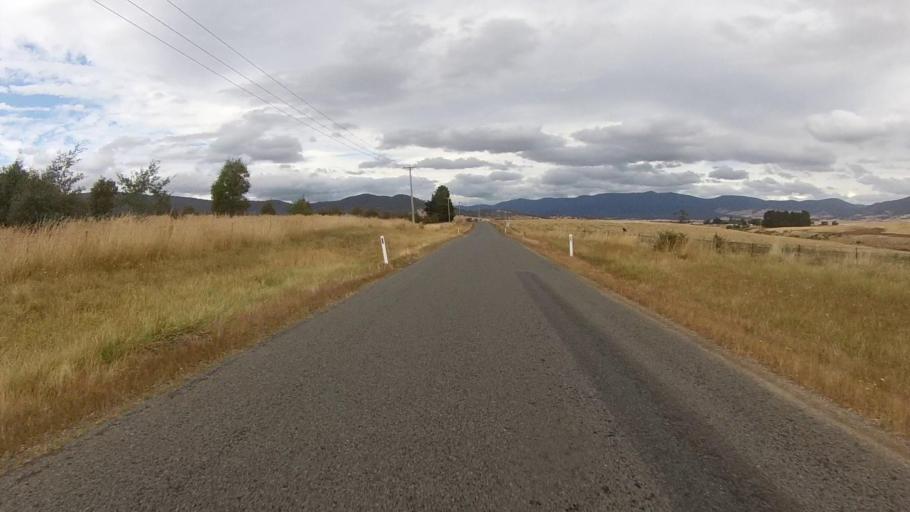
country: AU
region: Tasmania
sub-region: Northern Midlands
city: Evandale
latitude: -41.7851
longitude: 147.7285
